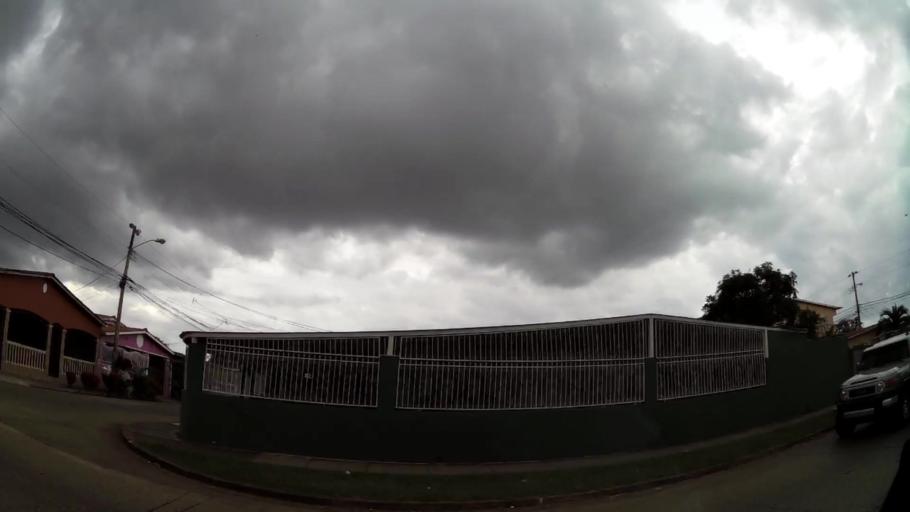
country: PA
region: Panama
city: Tocumen
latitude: 9.0522
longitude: -79.4097
